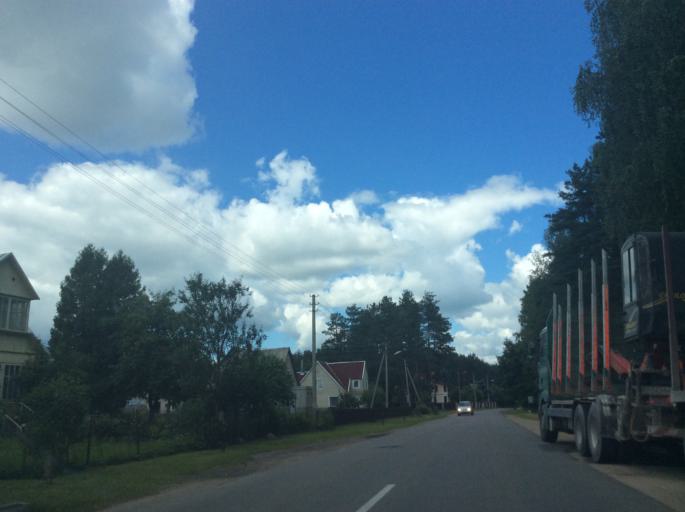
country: LT
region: Alytaus apskritis
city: Druskininkai
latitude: 54.0289
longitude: 23.9899
